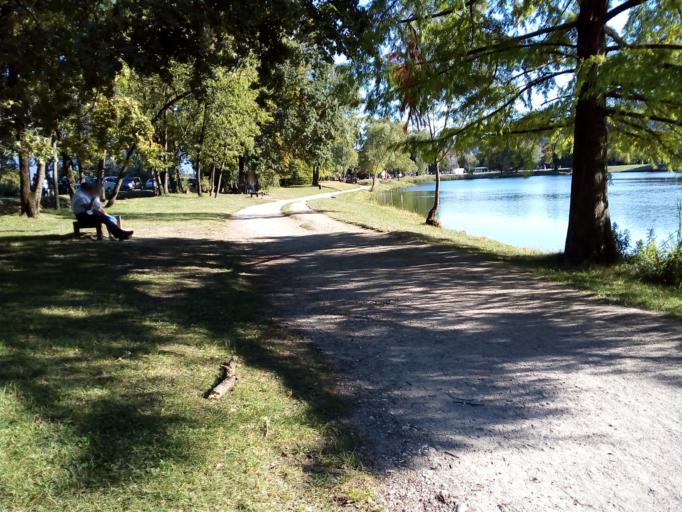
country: FR
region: Rhone-Alpes
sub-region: Departement de l'Isere
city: Sassenage
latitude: 45.2125
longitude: 5.6686
